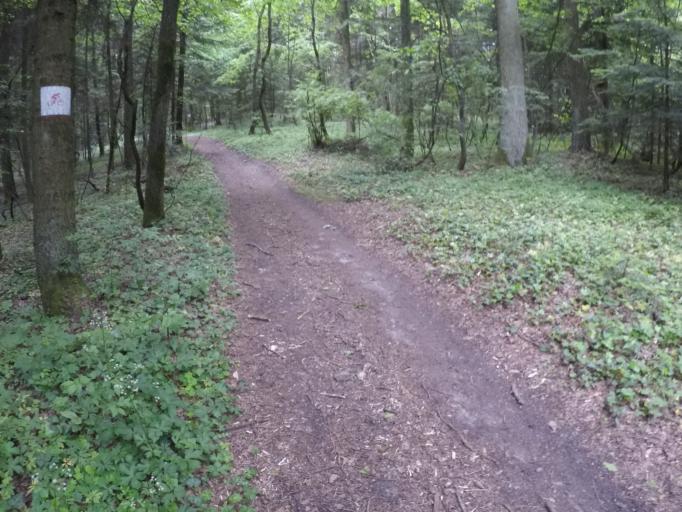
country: PL
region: Swietokrzyskie
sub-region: Powiat kielecki
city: Kielce
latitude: 50.8383
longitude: 20.6000
